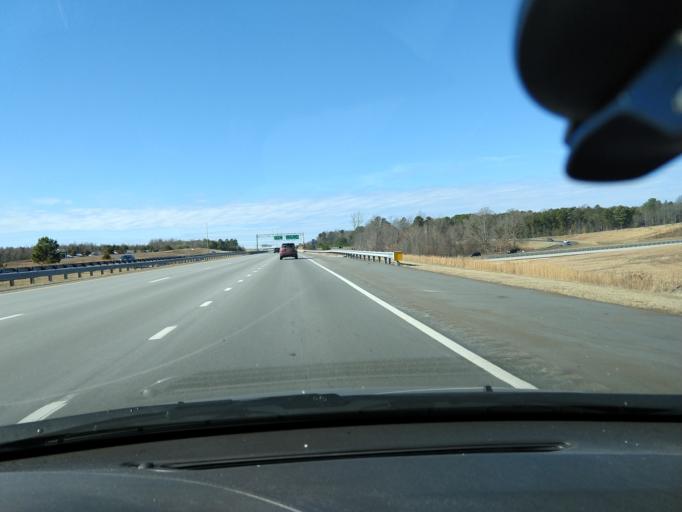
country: US
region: North Carolina
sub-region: Guilford County
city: Summerfield
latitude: 36.1165
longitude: -79.9060
